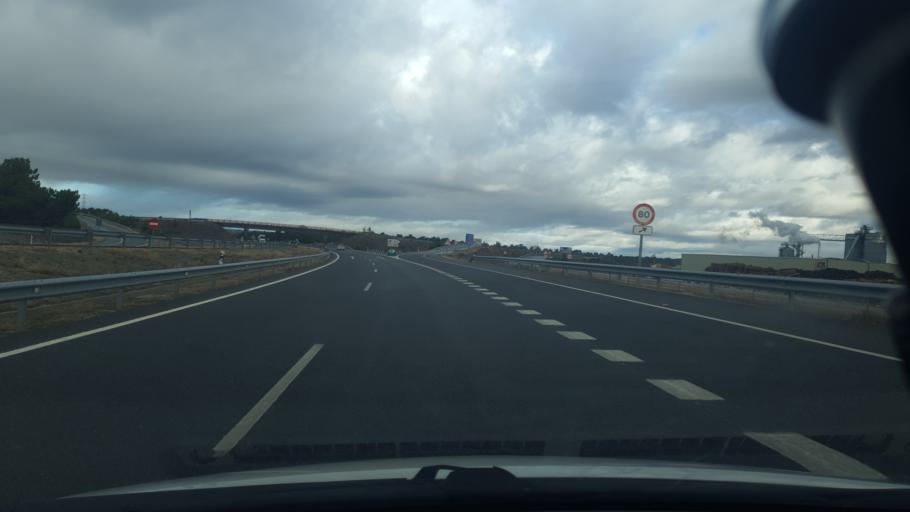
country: ES
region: Castille and Leon
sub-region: Provincia de Segovia
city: Sanchonuno
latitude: 41.3391
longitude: -4.3037
